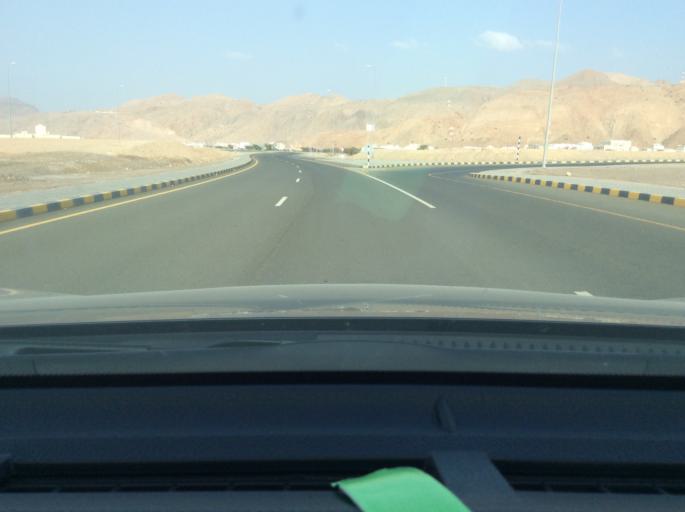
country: OM
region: Muhafazat Masqat
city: Bawshar
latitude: 23.5029
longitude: 58.5035
